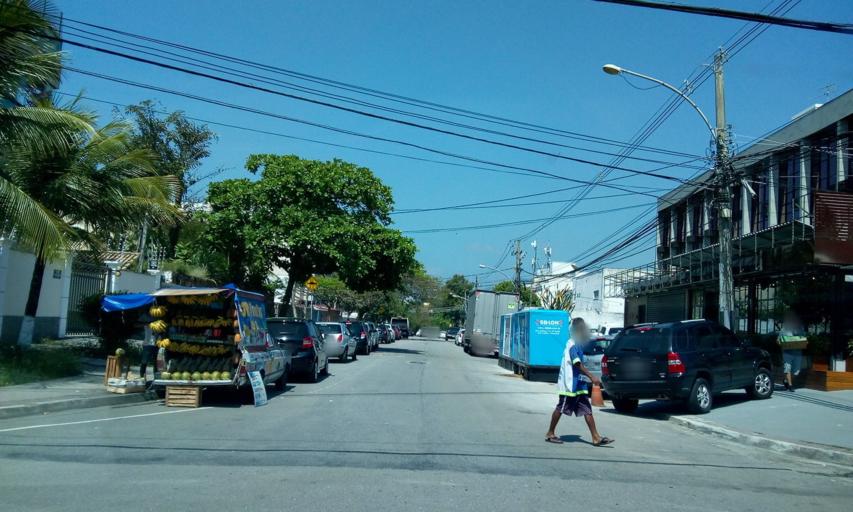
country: BR
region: Rio de Janeiro
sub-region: Nilopolis
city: Nilopolis
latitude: -23.0161
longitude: -43.4700
